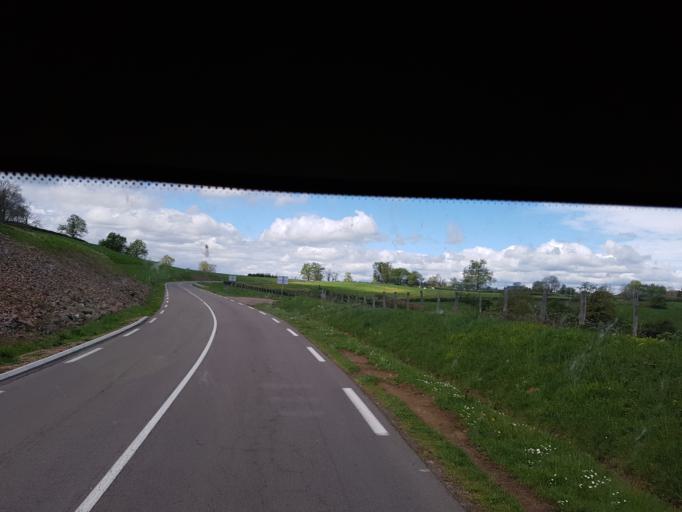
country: FR
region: Bourgogne
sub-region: Departement de Saone-et-Loire
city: La Clayette
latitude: 46.3146
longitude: 4.2923
